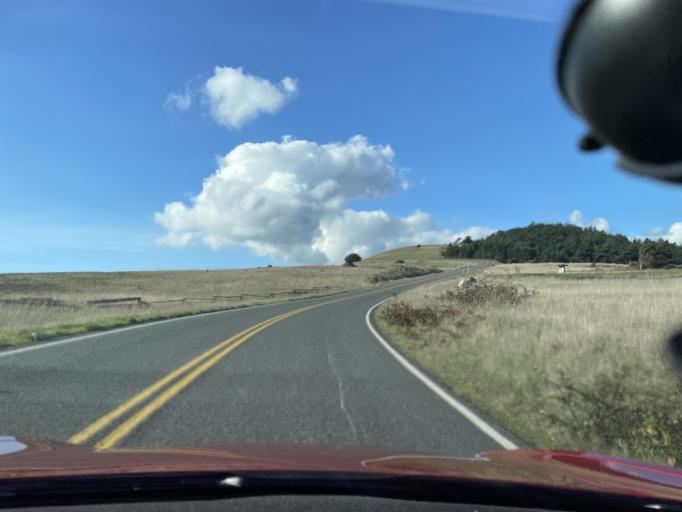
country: US
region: Washington
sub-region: San Juan County
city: Friday Harbor
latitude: 48.4529
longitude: -122.9684
